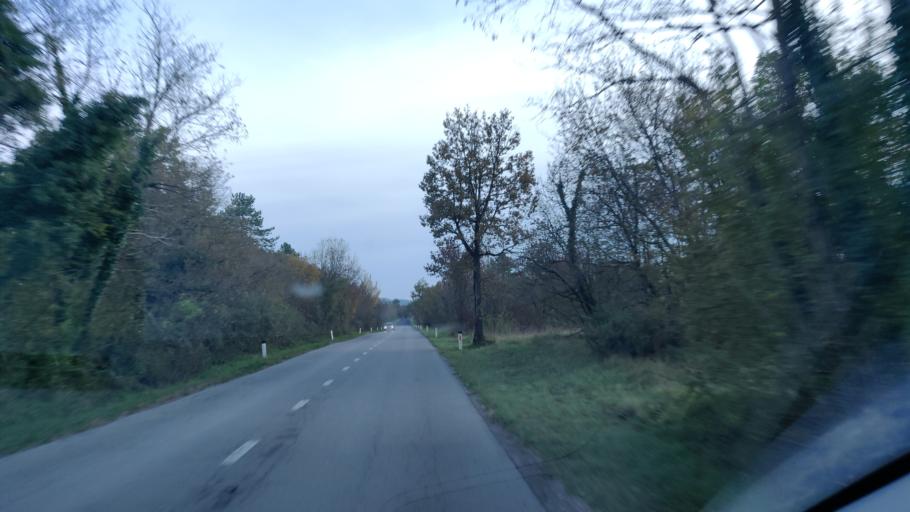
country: SI
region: Sezana
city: Sezana
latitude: 45.7561
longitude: 13.9170
